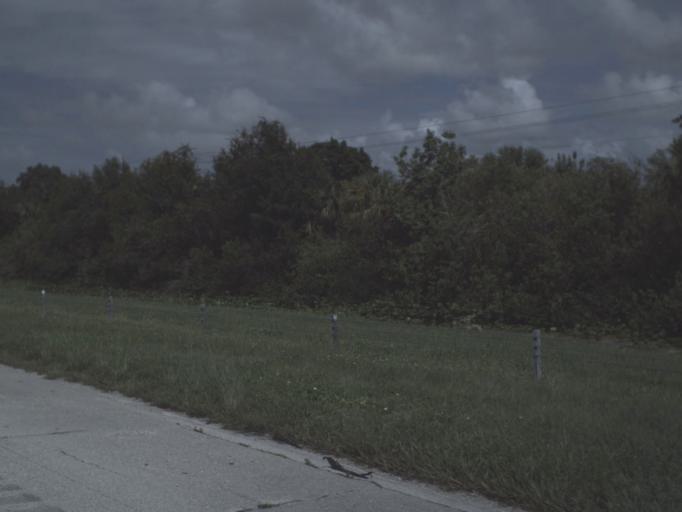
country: US
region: Florida
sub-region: Palm Beach County
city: Palm Beach Gardens
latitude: 26.8273
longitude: -80.1304
